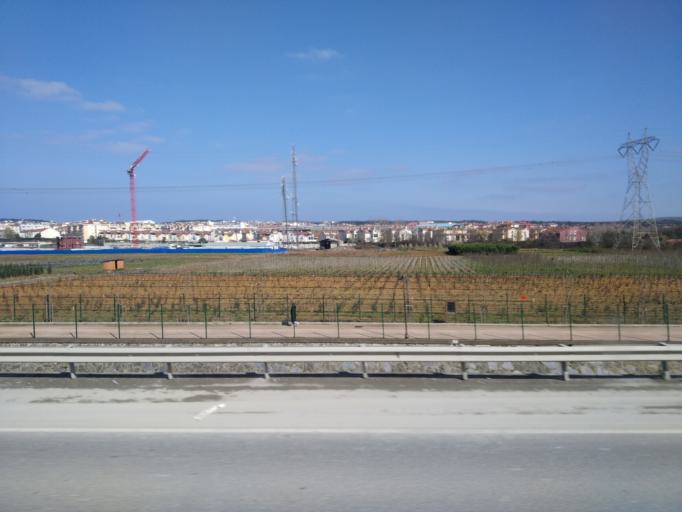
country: TR
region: Istanbul
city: Kemerburgaz
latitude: 41.1709
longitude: 28.8864
